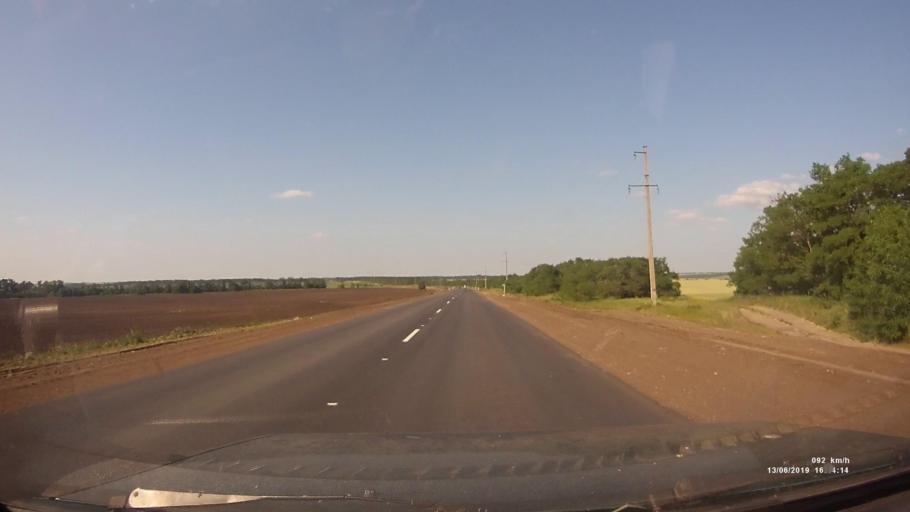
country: RU
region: Rostov
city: Kazanskaya
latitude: 49.8694
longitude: 41.2898
